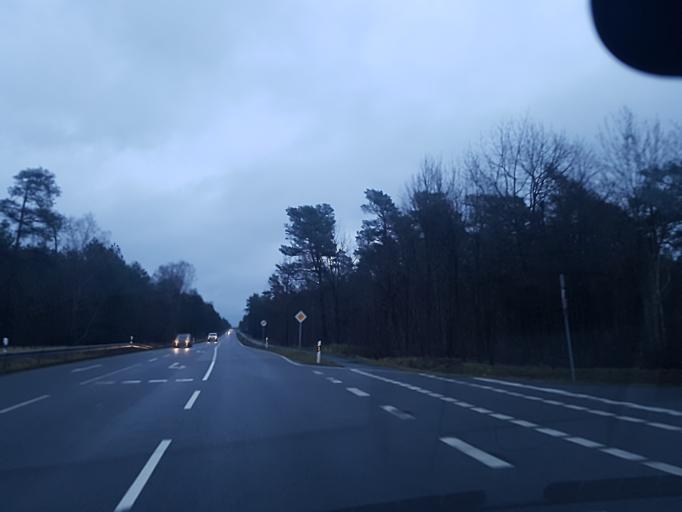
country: DE
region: Brandenburg
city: Schonewalde
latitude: 51.6349
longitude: 13.6362
